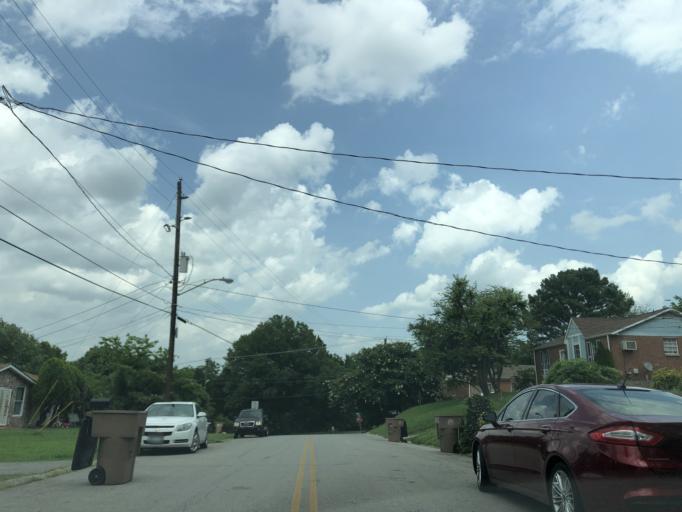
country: US
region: Tennessee
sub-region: Williamson County
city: Brentwood Estates
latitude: 36.0613
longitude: -86.6833
